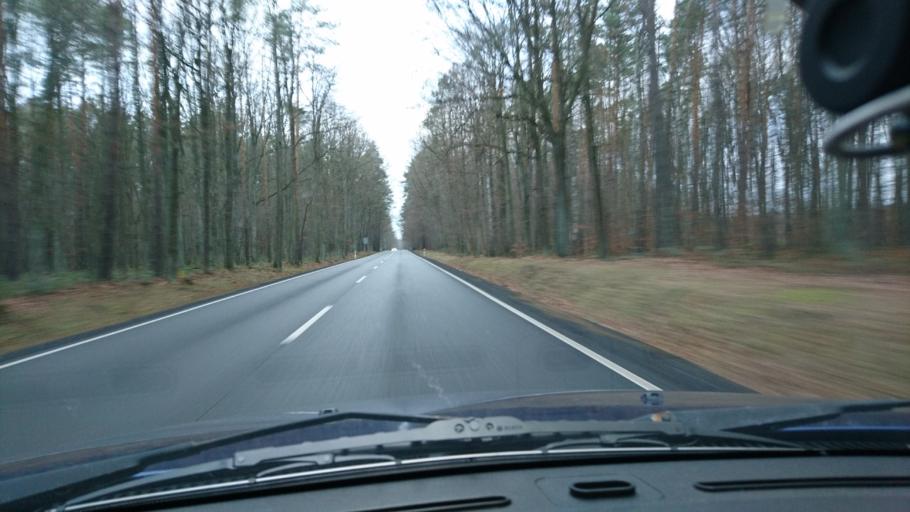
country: PL
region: Opole Voivodeship
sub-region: Powiat oleski
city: Olesno
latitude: 50.9256
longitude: 18.3367
